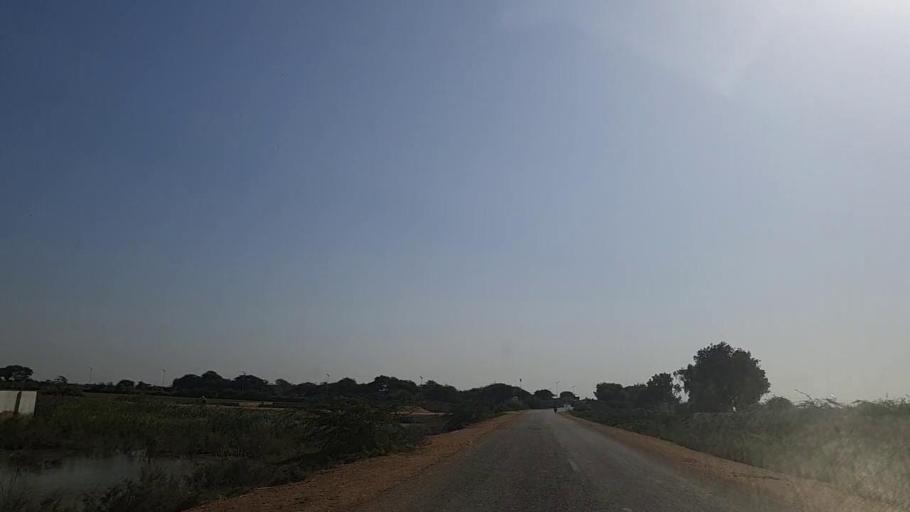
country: PK
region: Sindh
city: Jati
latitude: 24.4262
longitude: 68.2580
